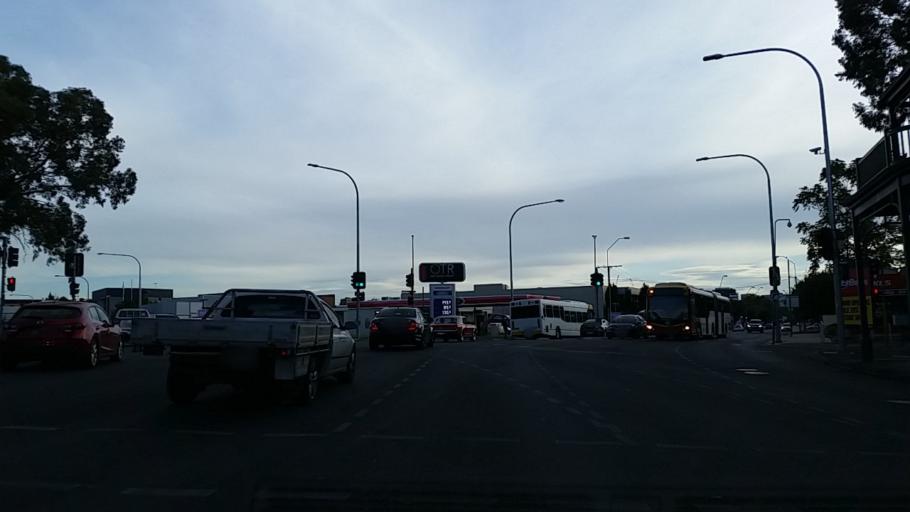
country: AU
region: South Australia
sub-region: Norwood Payneham St Peters
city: Trinity Gardens
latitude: -34.9154
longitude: 138.6229
